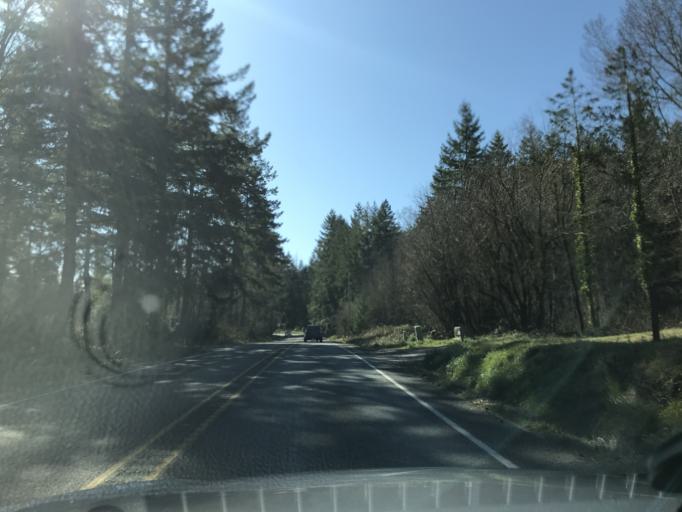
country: US
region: Washington
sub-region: Pierce County
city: Key Center
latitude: 47.3485
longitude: -122.7393
